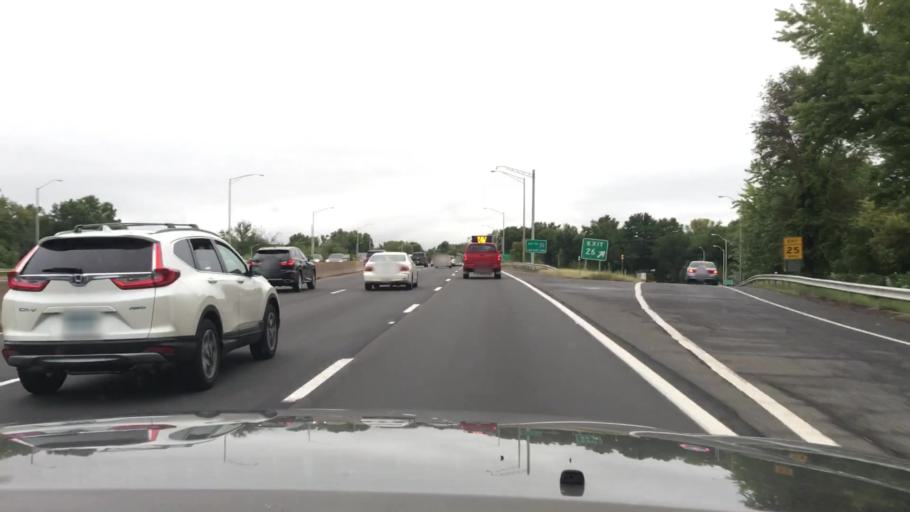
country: US
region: Connecticut
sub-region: Hartford County
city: Wethersfield
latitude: 41.7159
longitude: -72.6492
